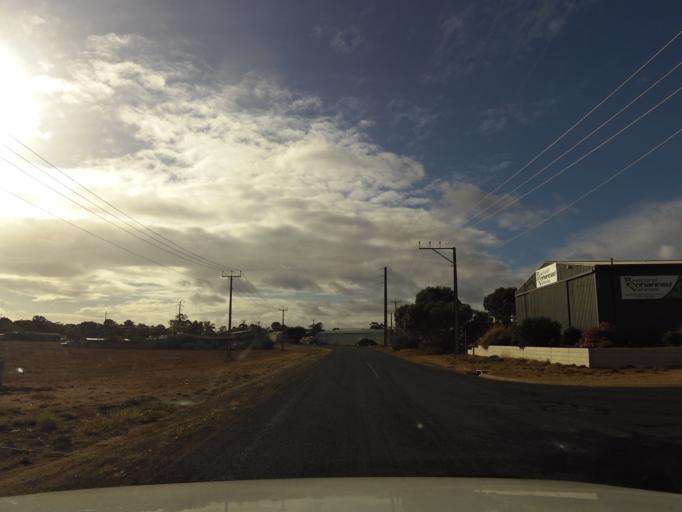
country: AU
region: South Australia
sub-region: Berri and Barmera
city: Berri
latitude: -34.2694
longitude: 140.5997
